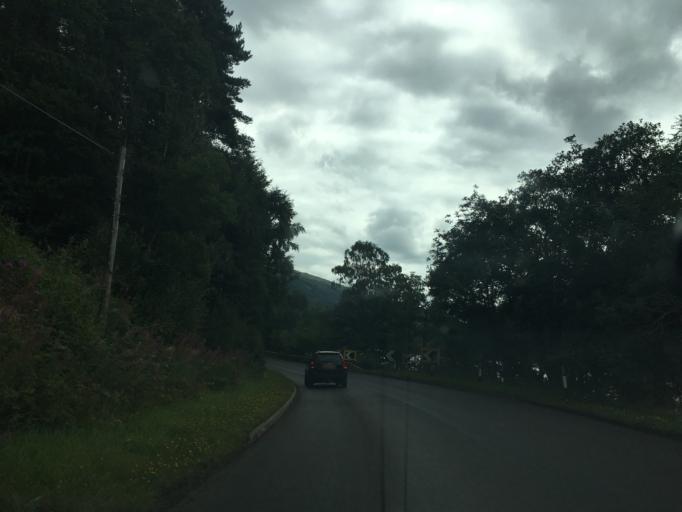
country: GB
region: Scotland
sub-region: Stirling
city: Callander
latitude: 56.2970
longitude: -4.3028
